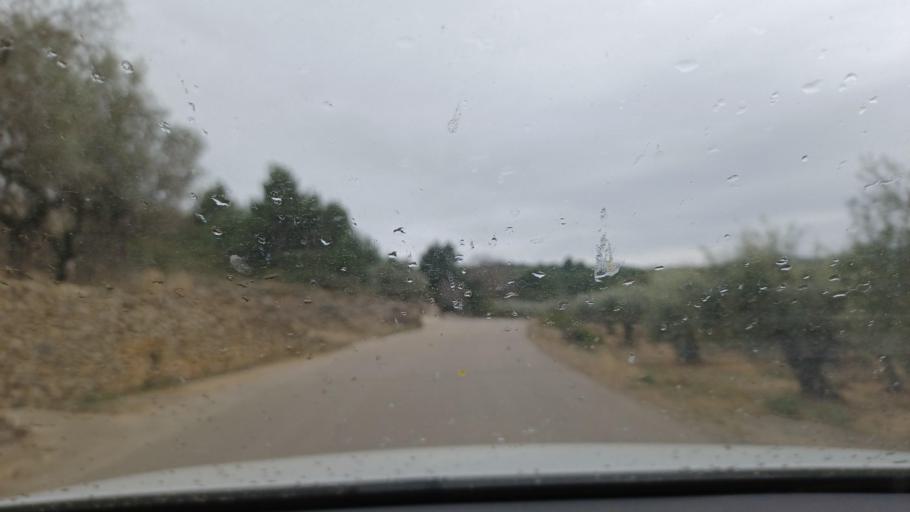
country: ES
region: Valencia
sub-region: Provincia de Castello
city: Traiguera
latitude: 40.5085
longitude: 0.2946
